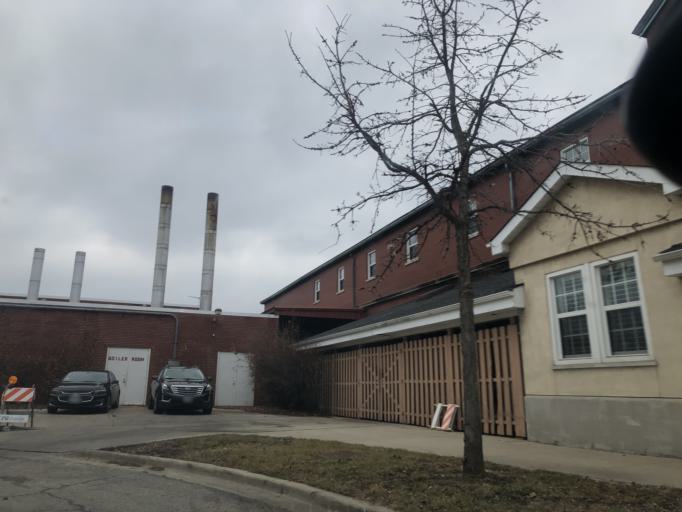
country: US
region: Illinois
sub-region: Cook County
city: Evanston
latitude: 41.9955
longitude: -87.6783
